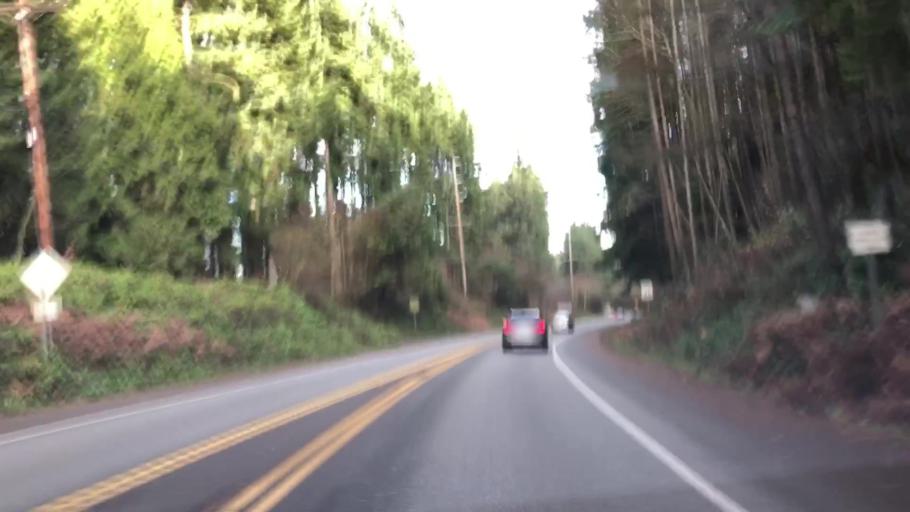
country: US
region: Washington
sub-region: Kitsap County
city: Suquamish
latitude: 47.7064
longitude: -122.5609
